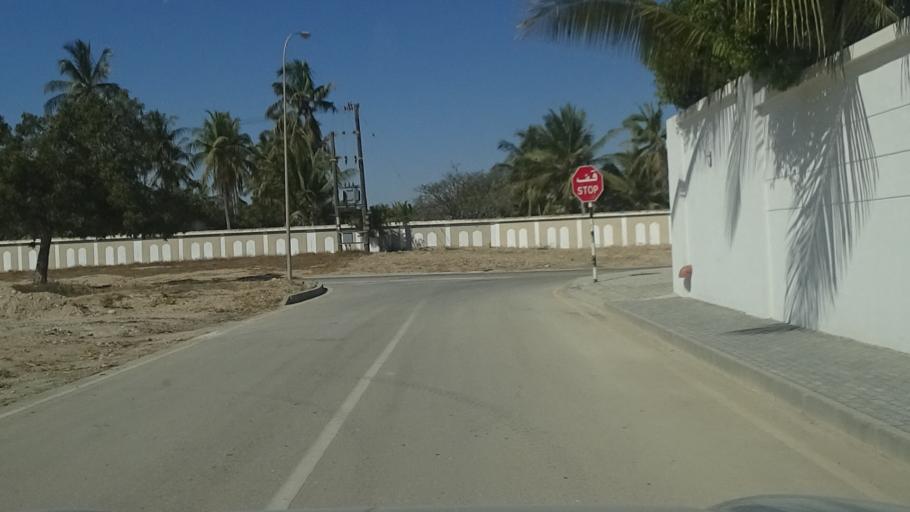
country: OM
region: Zufar
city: Salalah
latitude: 17.0328
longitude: 54.1542
